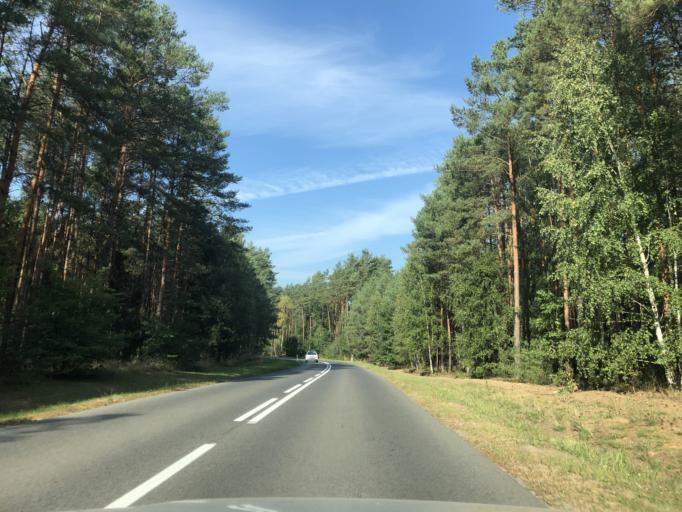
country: PL
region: Greater Poland Voivodeship
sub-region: Powiat pilski
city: Kaczory
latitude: 53.1172
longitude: 16.8296
